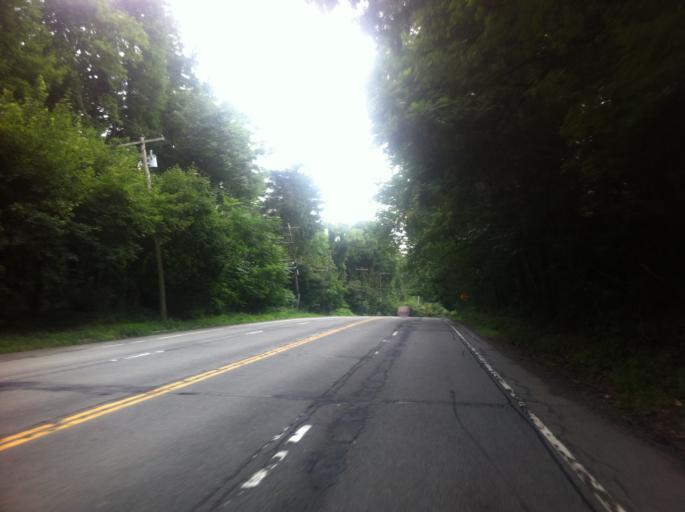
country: US
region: New York
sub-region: Nassau County
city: Upper Brookville
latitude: 40.8352
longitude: -73.5664
